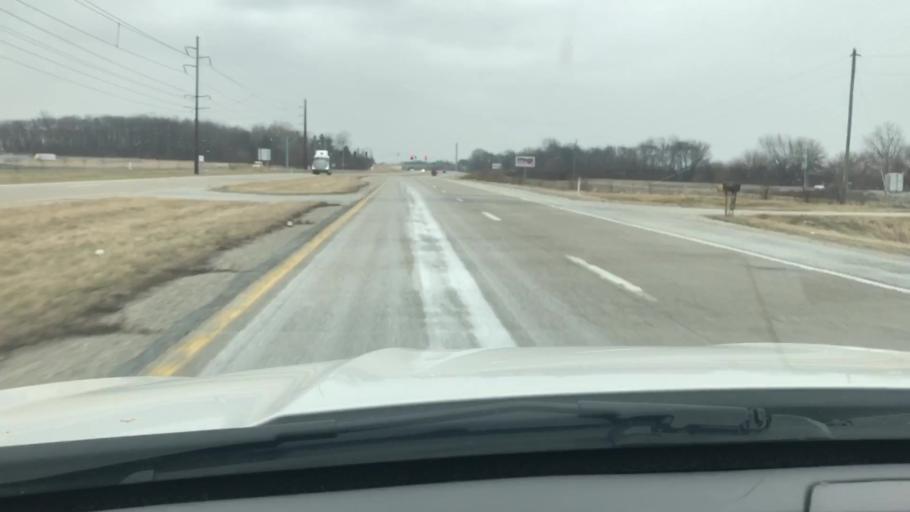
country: US
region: Indiana
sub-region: Tippecanoe County
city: Dayton
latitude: 40.3743
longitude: -86.7956
